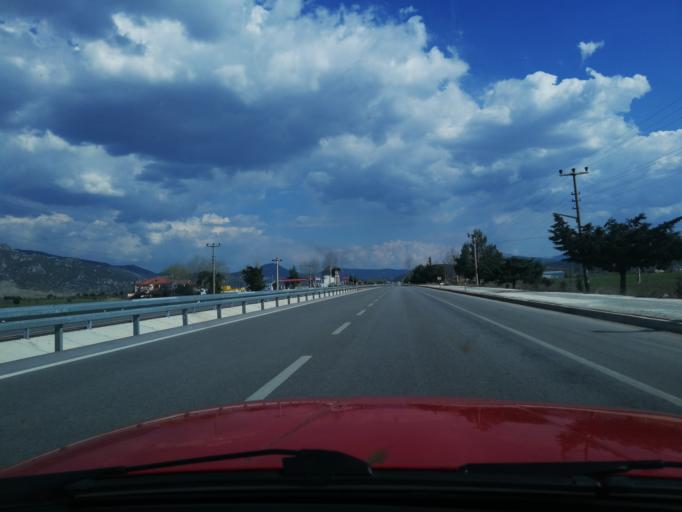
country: TR
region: Burdur
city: Celtikci
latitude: 37.5281
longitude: 30.4980
